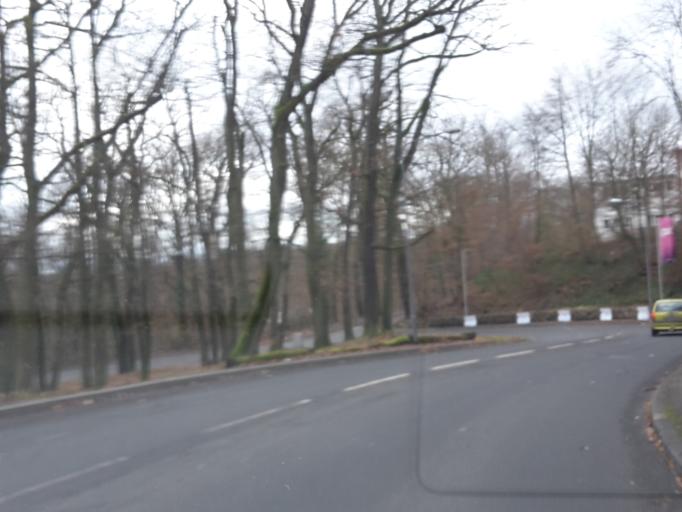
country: DE
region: Hesse
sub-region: Regierungsbezirk Darmstadt
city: Wiesbaden
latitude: 50.0949
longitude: 8.2172
